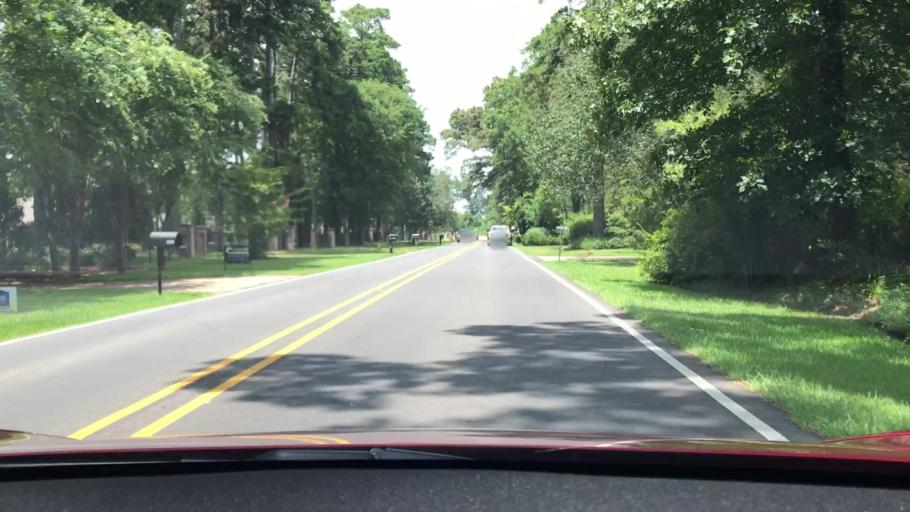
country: US
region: Louisiana
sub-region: Bossier Parish
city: Bossier City
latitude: 32.3808
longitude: -93.7138
